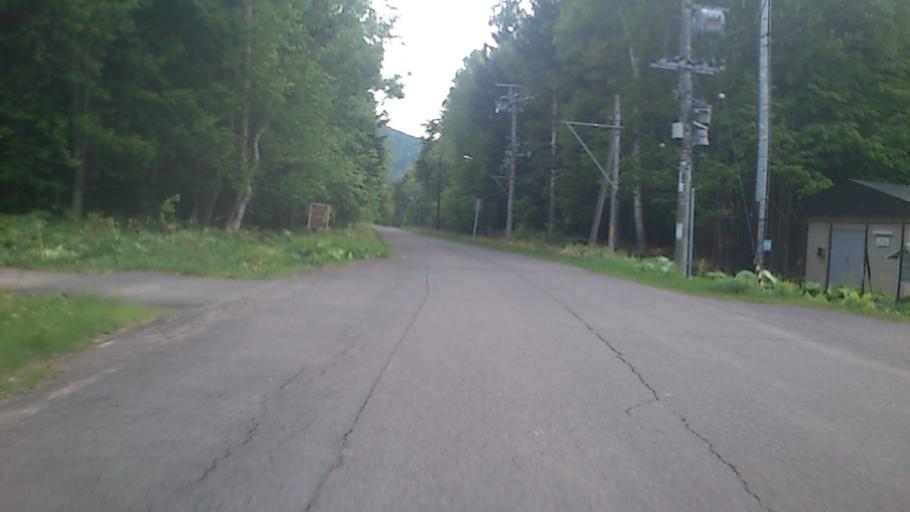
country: JP
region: Hokkaido
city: Bihoro
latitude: 43.4328
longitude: 144.0875
